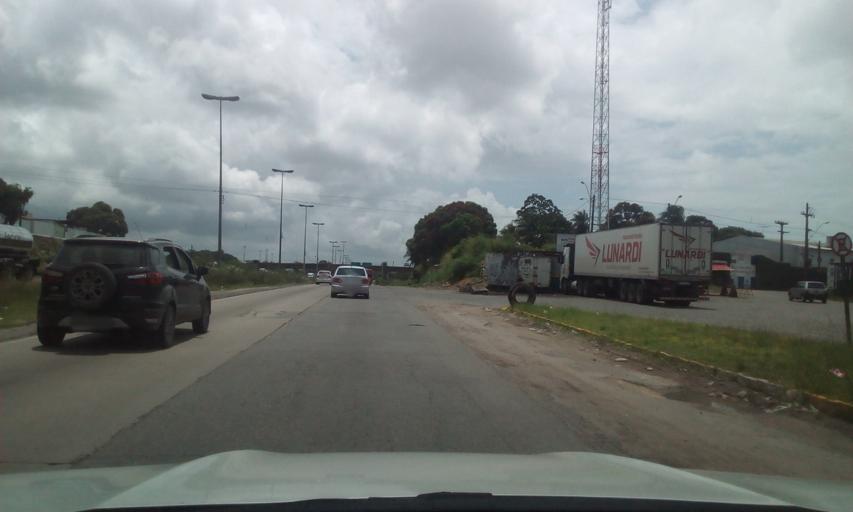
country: BR
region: Pernambuco
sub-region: Recife
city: Recife
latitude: -8.0786
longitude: -34.9429
